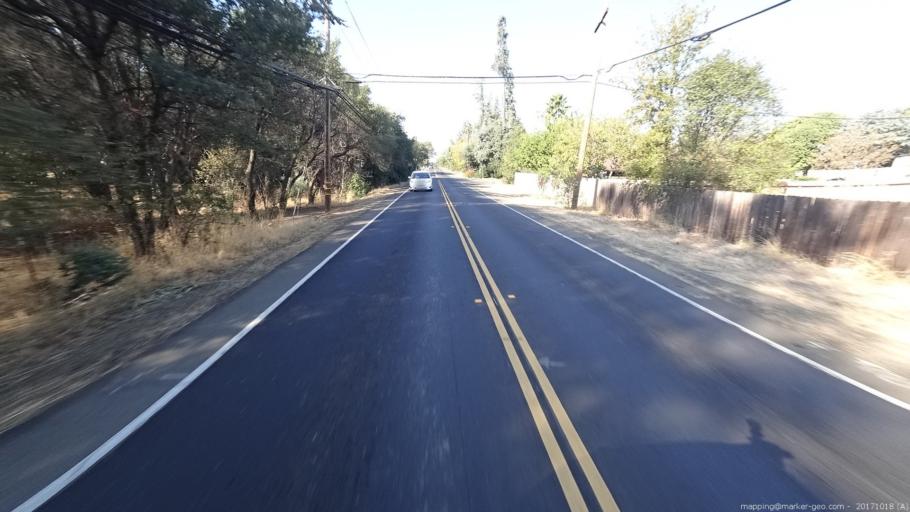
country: US
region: California
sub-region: Shasta County
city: Redding
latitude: 40.5347
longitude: -122.3265
